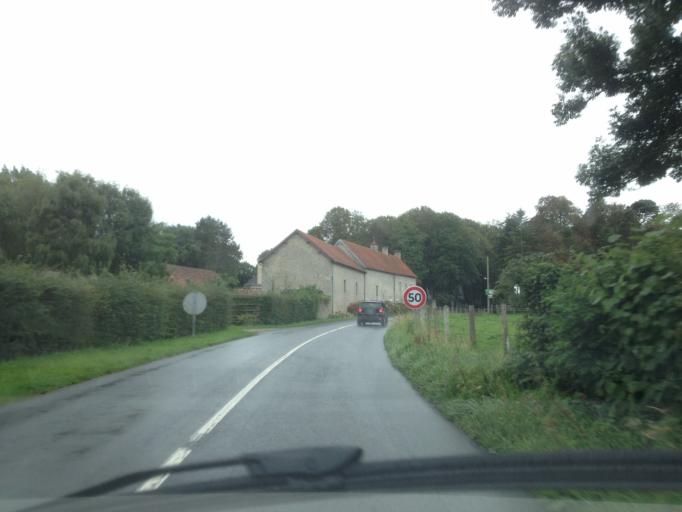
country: FR
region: Lower Normandy
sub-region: Departement du Calvados
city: Saint-Vigor-le-Grand
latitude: 49.3309
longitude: -0.6397
